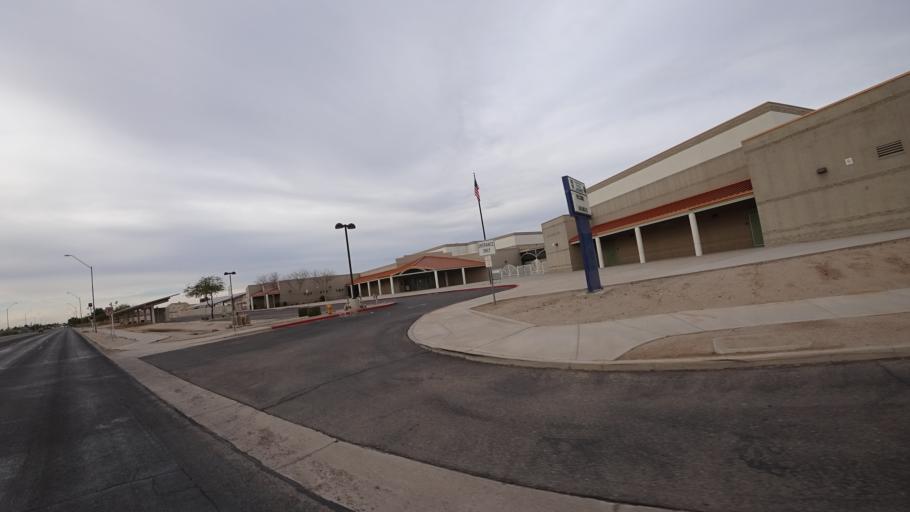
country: US
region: Arizona
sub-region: Maricopa County
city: El Mirage
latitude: 33.6162
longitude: -112.3136
